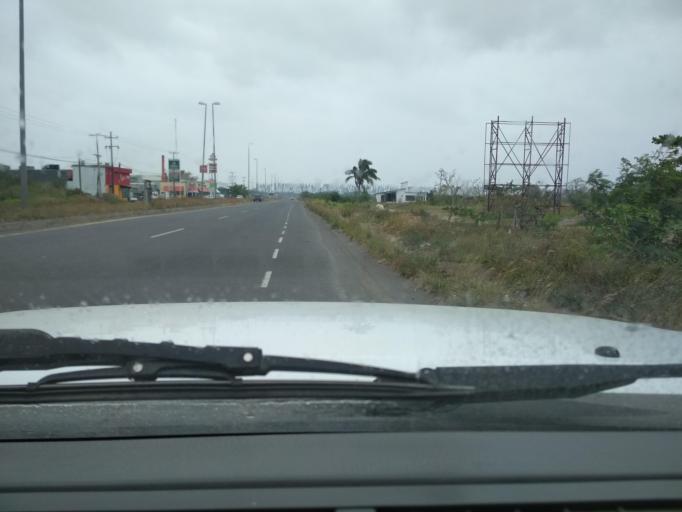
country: MX
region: Veracruz
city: Paso del Toro
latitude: 19.0418
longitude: -96.1351
